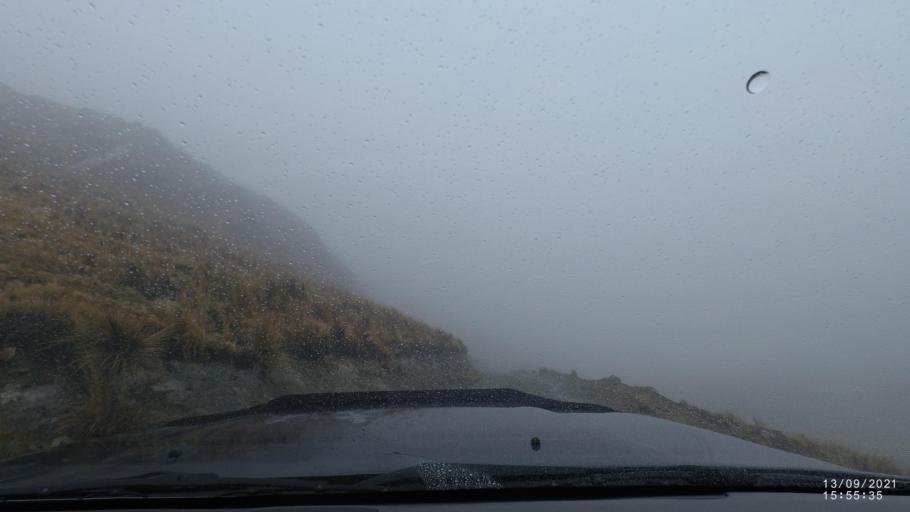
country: BO
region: Cochabamba
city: Colomi
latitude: -17.3061
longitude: -65.7057
